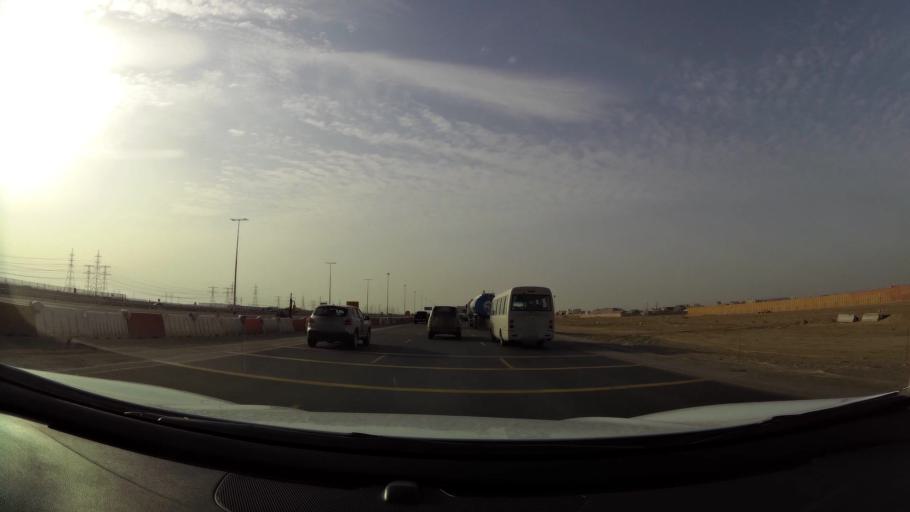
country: AE
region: Abu Dhabi
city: Abu Dhabi
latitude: 24.2990
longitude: 54.5406
